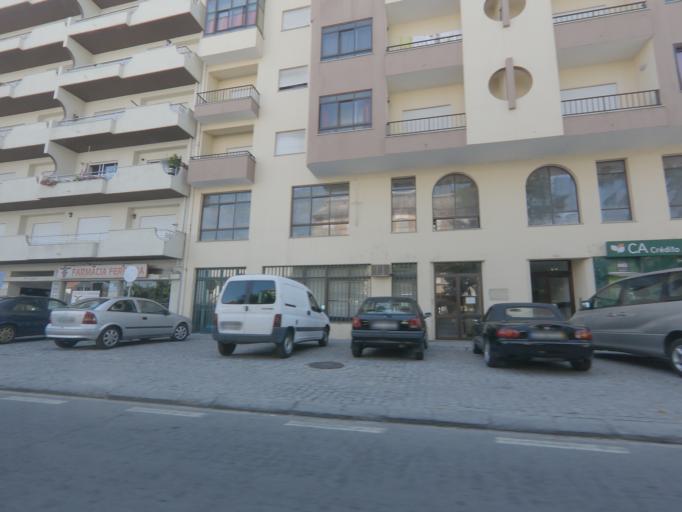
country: PT
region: Viseu
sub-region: Moimenta da Beira
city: Moimenta da Beira
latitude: 40.9784
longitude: -7.6127
